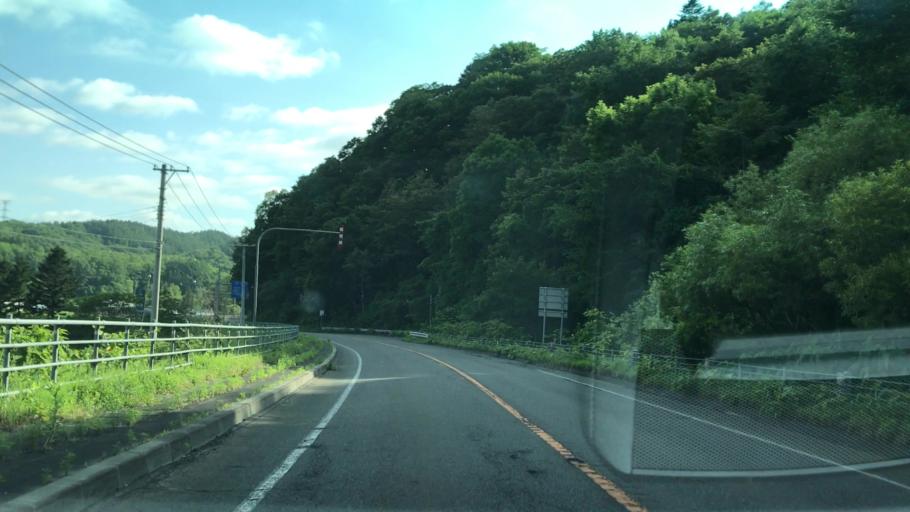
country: JP
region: Hokkaido
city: Chitose
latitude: 42.8724
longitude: 142.1641
